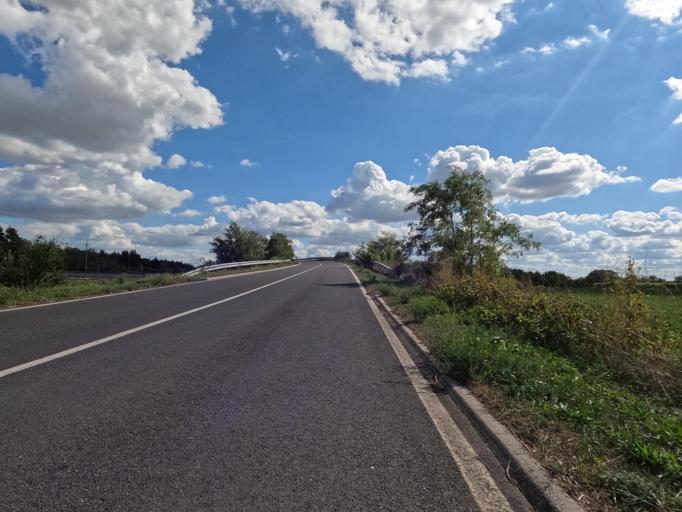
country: HU
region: Tolna
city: Paks
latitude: 46.5902
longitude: 18.8132
